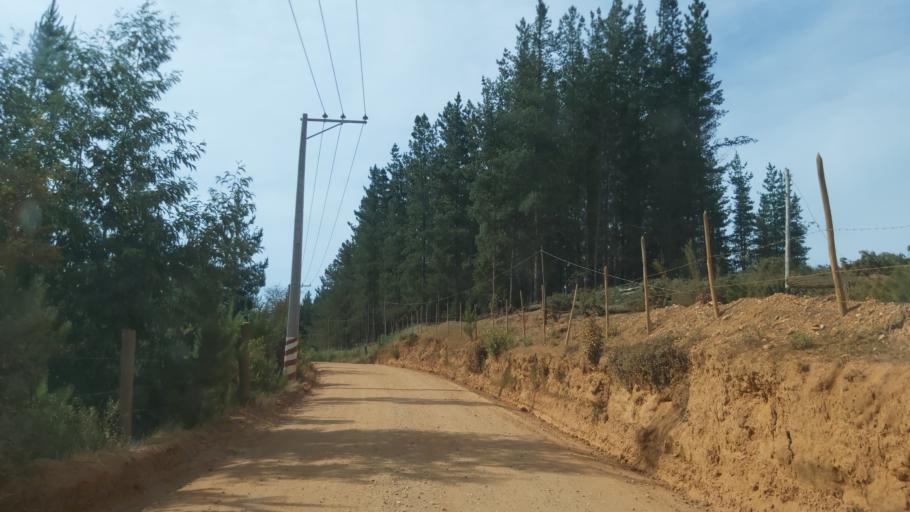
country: CL
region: Maule
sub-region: Provincia de Talca
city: Constitucion
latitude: -34.8495
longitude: -72.0338
